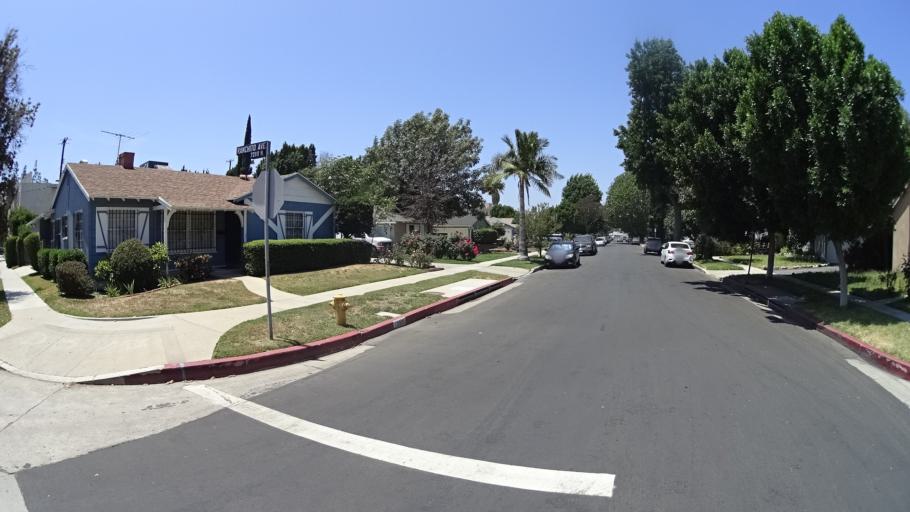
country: US
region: California
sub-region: Los Angeles County
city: Van Nuys
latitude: 34.2022
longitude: -118.4358
